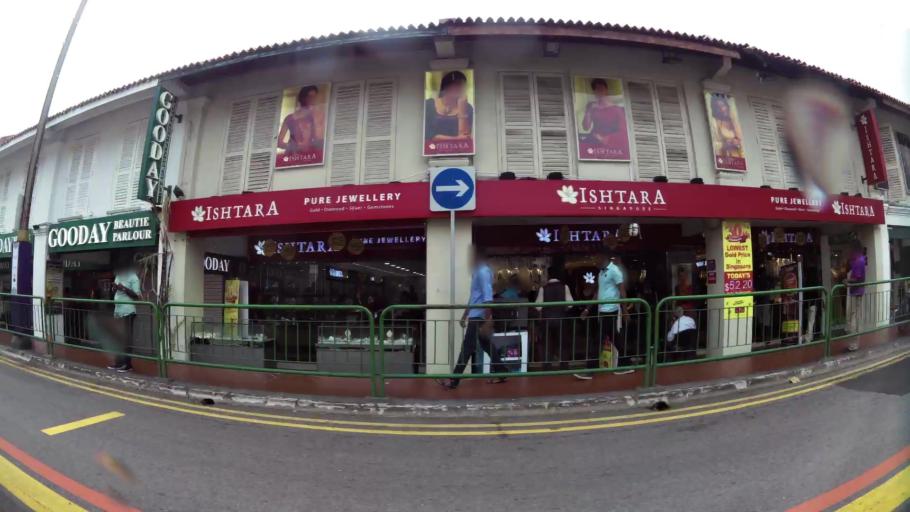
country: SG
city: Singapore
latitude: 1.3073
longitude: 103.8523
